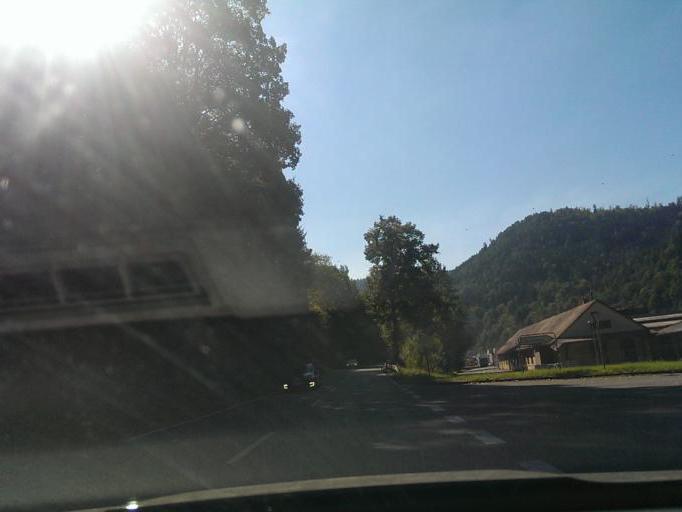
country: DE
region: Baden-Wuerttemberg
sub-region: Karlsruhe Region
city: Hofen an der Enz
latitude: 48.7964
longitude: 8.5827
